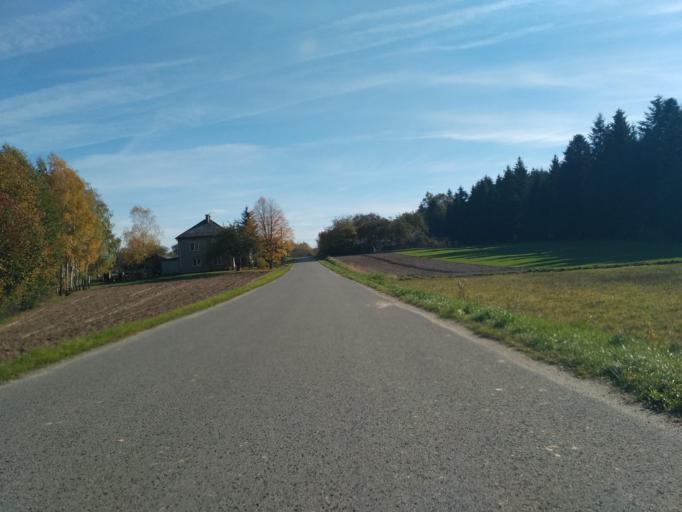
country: PL
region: Subcarpathian Voivodeship
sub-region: Powiat ropczycko-sedziszowski
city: Zagorzyce
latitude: 49.9971
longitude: 21.7132
